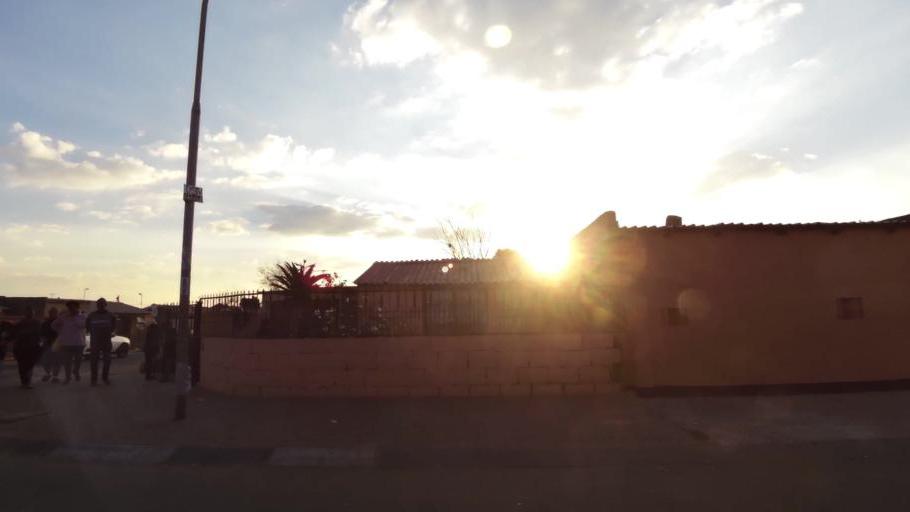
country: ZA
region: Gauteng
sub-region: City of Johannesburg Metropolitan Municipality
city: Roodepoort
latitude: -26.2122
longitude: 27.8967
